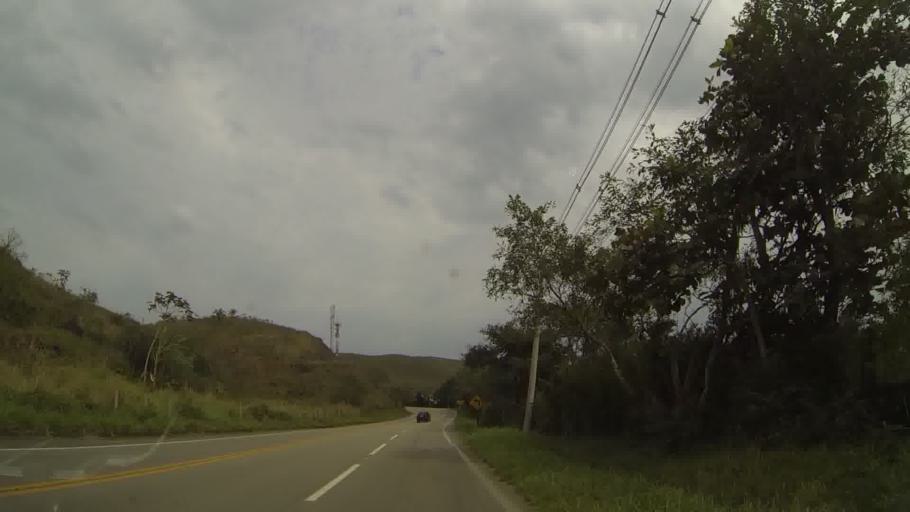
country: BR
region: Sao Paulo
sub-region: Sao Sebastiao
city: Sao Sebastiao
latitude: -23.8019
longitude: -45.5452
